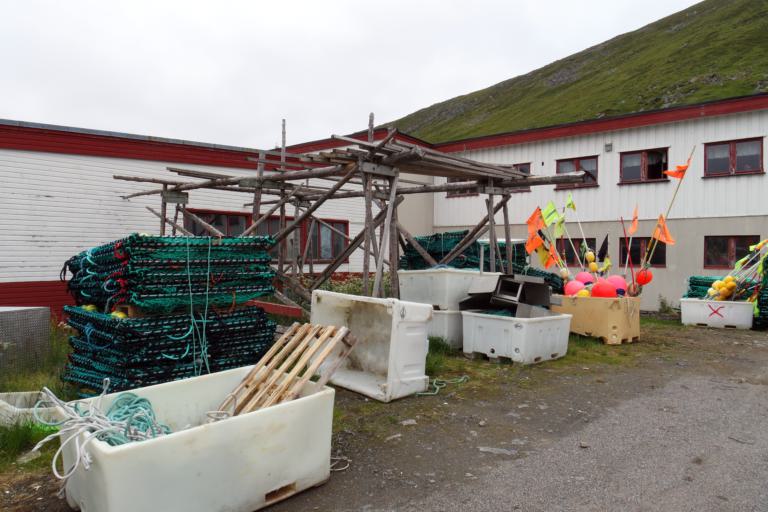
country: NO
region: Finnmark Fylke
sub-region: Nordkapp
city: Honningsvag
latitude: 71.1141
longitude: 25.8339
